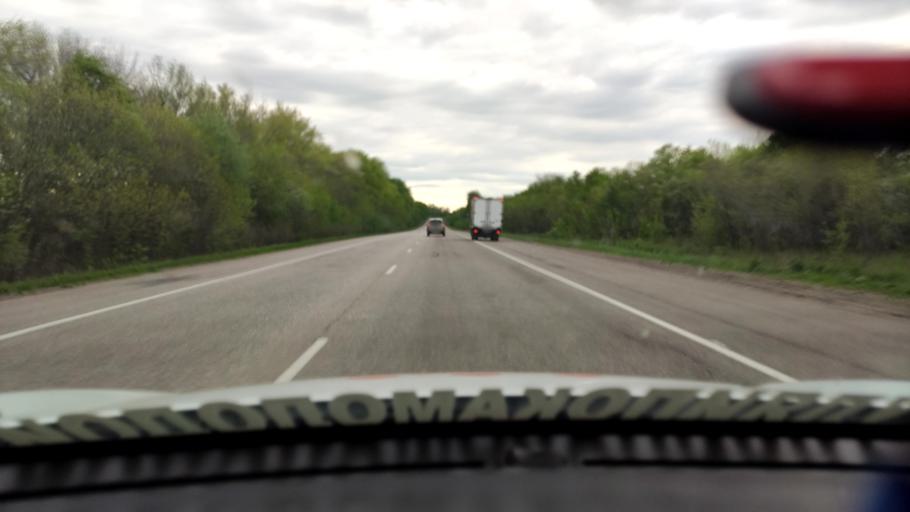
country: RU
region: Voronezj
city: Kolodeznyy
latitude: 51.2795
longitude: 39.0442
